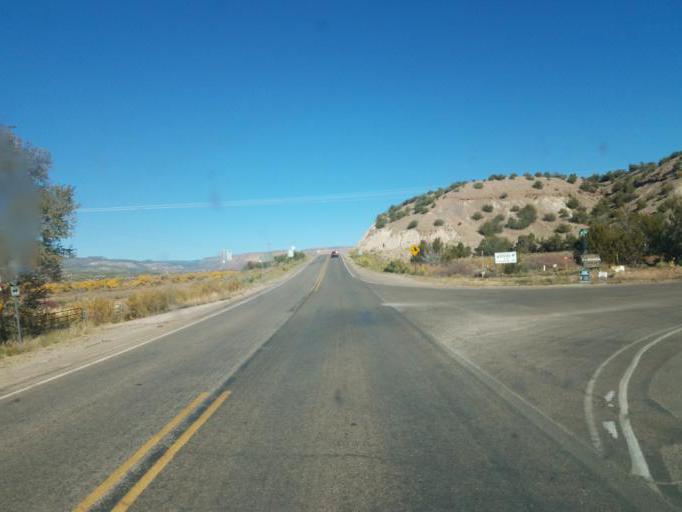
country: US
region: New Mexico
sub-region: Sandoval County
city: Jemez Pueblo
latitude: 35.6255
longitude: -106.7242
